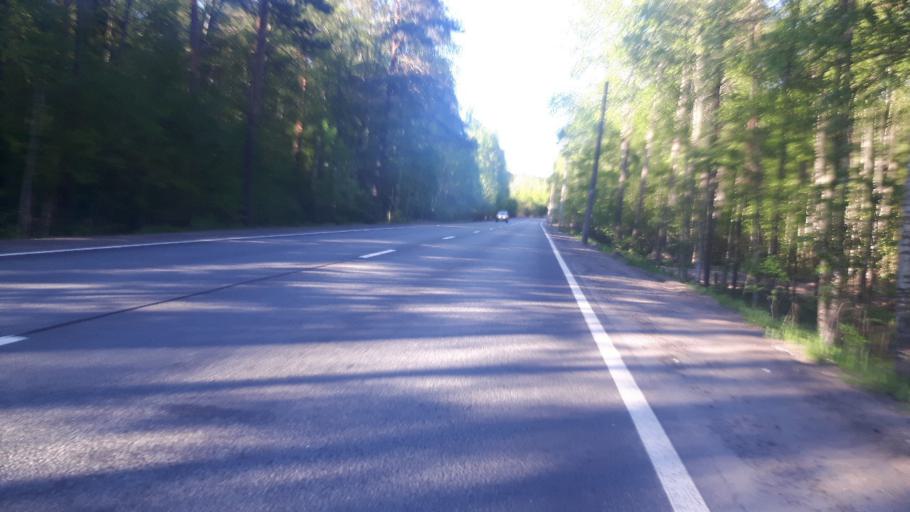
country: RU
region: Leningrad
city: Molodezhnoye
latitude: 60.1783
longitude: 29.4476
